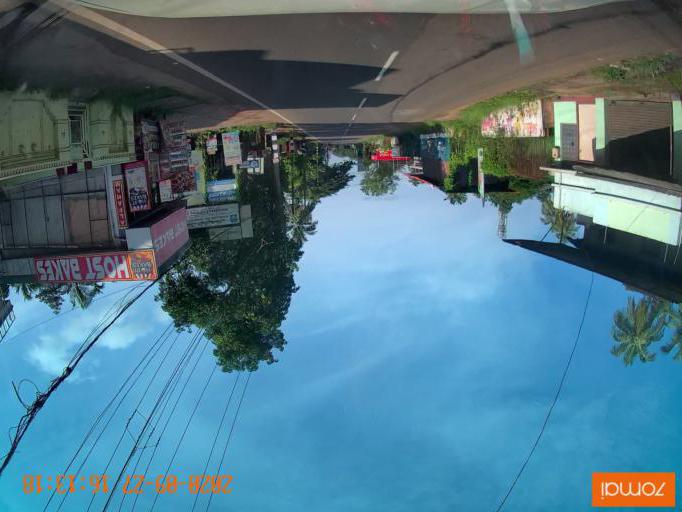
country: IN
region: Kerala
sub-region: Thrissur District
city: Trichur
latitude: 10.4712
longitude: 76.2428
